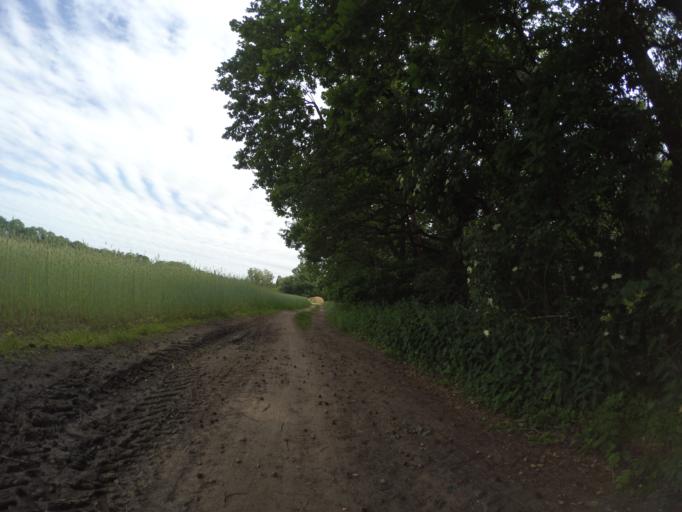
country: CZ
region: Central Bohemia
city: Prerov nad Labem
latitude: 50.1822
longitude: 14.8031
